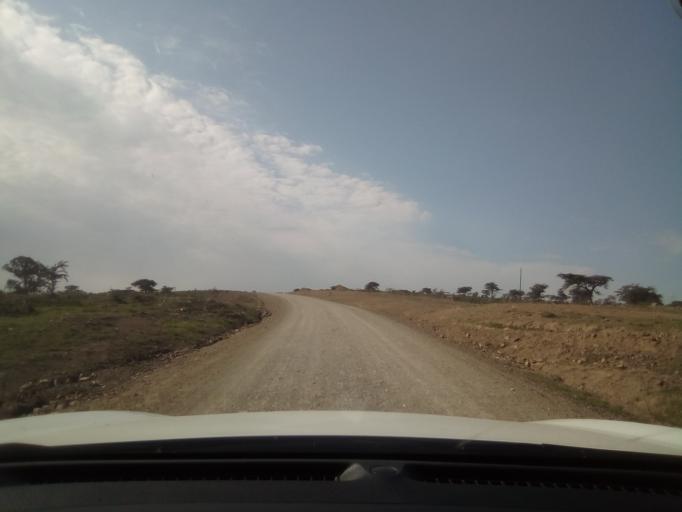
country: ZA
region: Eastern Cape
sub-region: Buffalo City Metropolitan Municipality
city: Bhisho
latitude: -32.9872
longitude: 27.2510
